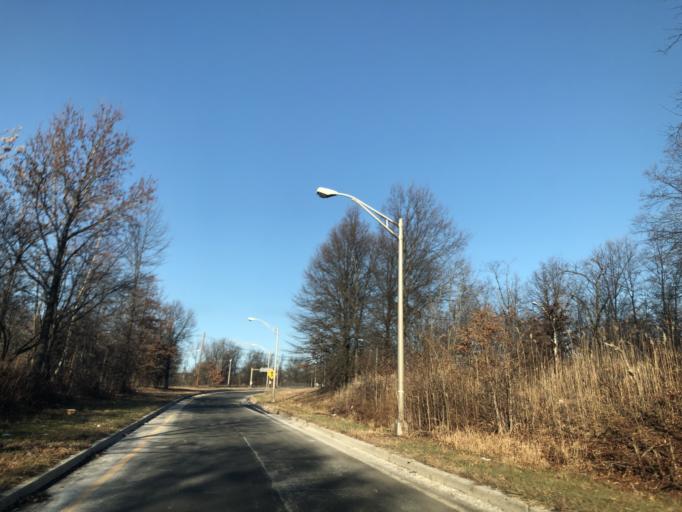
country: US
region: New Jersey
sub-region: Middlesex County
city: Fords
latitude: 40.5204
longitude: -74.3127
